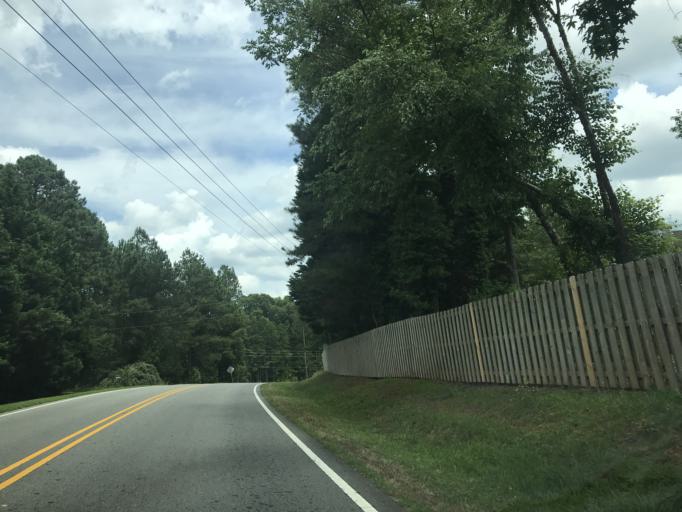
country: US
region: North Carolina
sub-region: Wake County
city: West Raleigh
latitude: 35.9137
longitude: -78.6918
